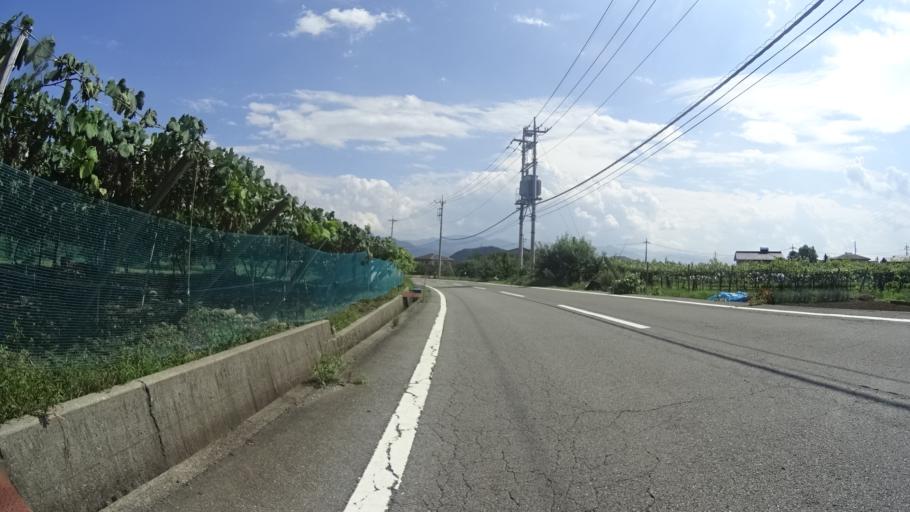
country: JP
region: Yamanashi
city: Enzan
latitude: 35.7306
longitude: 138.7224
